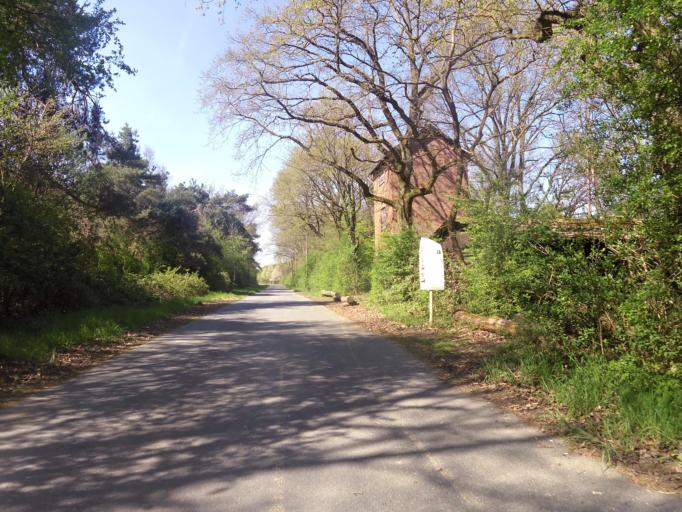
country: DE
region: Hesse
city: Morfelden-Walldorf
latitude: 49.9838
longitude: 8.5926
